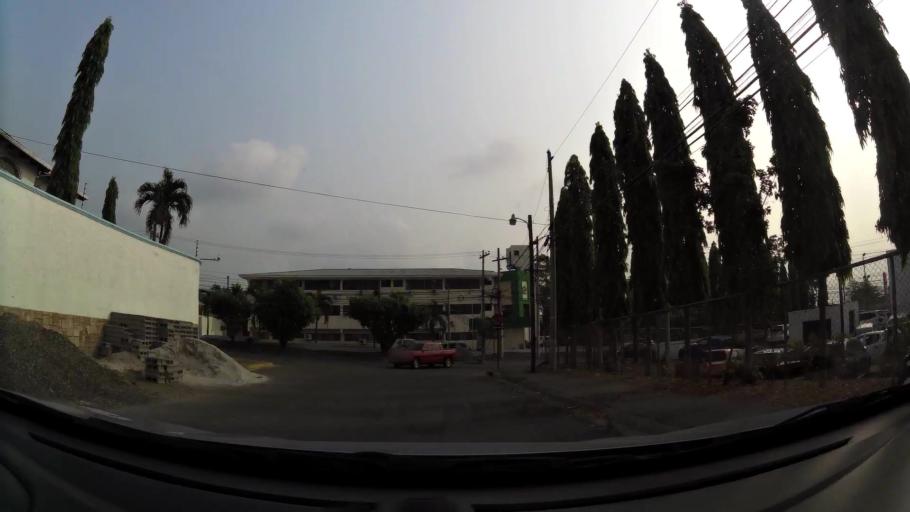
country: HN
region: Cortes
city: Armenta
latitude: 15.4865
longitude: -88.0352
